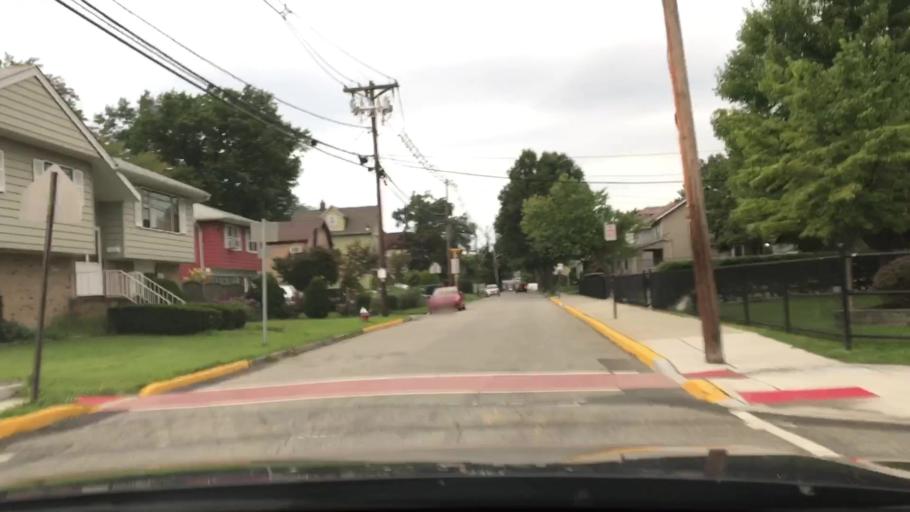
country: US
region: New Jersey
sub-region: Bergen County
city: Bergenfield
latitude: 40.9259
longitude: -73.9933
